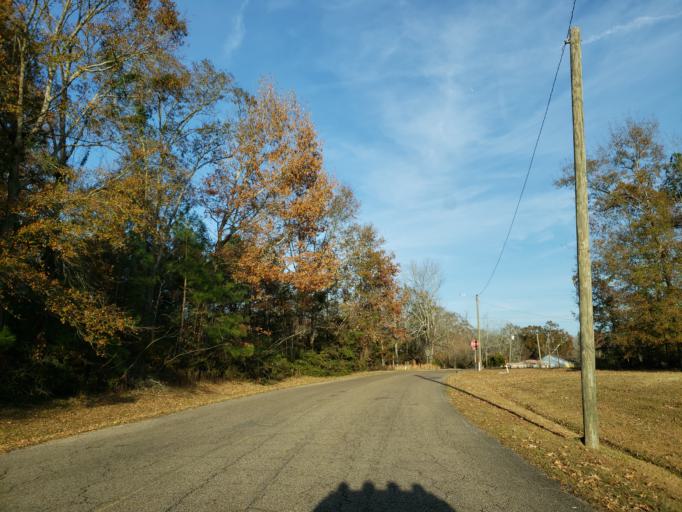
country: US
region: Mississippi
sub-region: Forrest County
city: Hattiesburg
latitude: 31.2988
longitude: -89.3156
